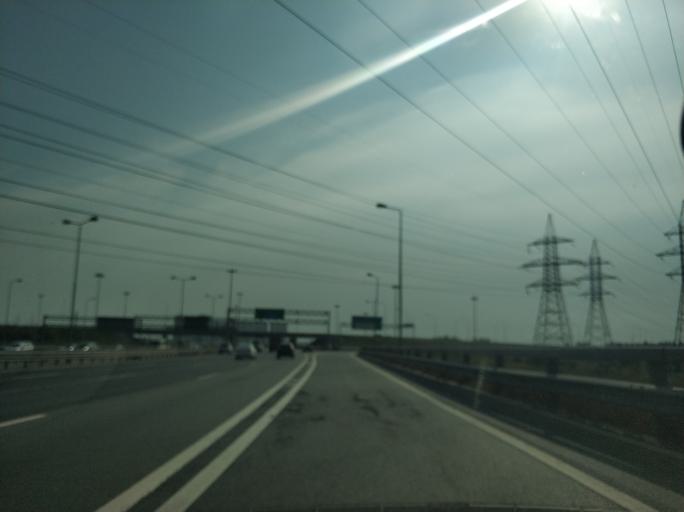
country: RU
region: Leningrad
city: Murino
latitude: 60.0192
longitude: 30.4568
